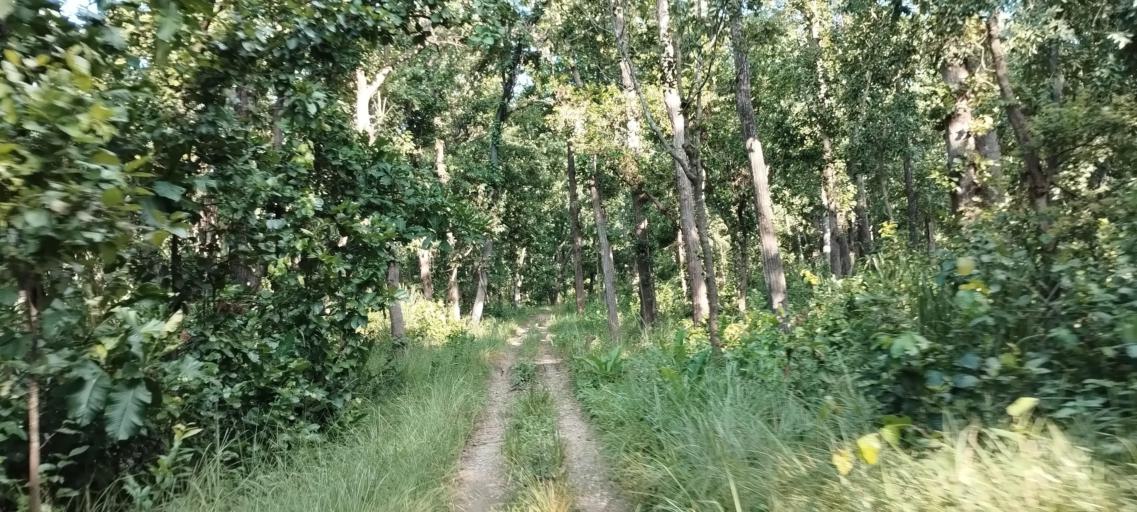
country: NP
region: Far Western
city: Tikapur
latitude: 28.5211
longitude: 81.2731
